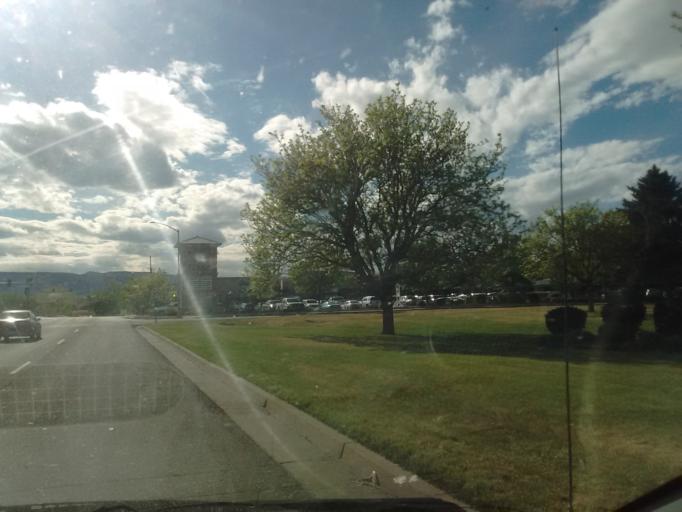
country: US
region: Colorado
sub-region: Mesa County
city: Grand Junction
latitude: 39.0704
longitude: -108.5717
